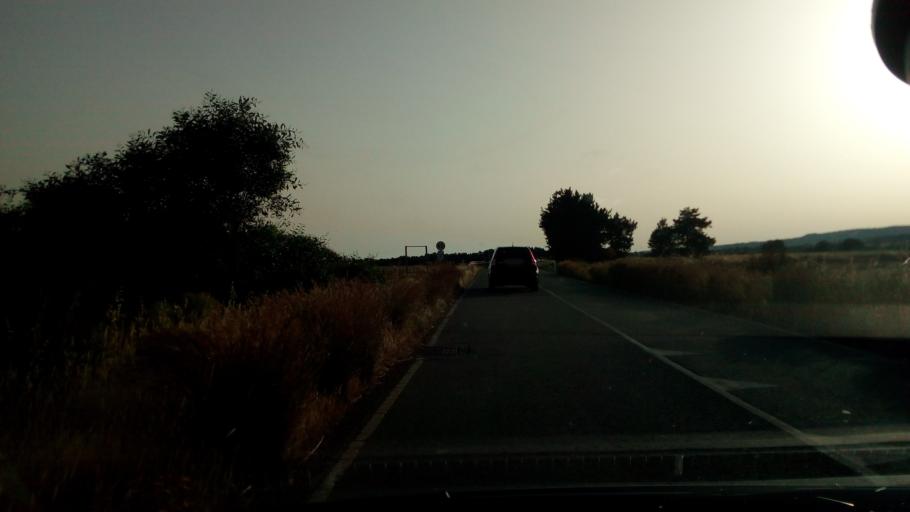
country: CY
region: Larnaka
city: Kofinou
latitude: 34.7759
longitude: 33.4597
